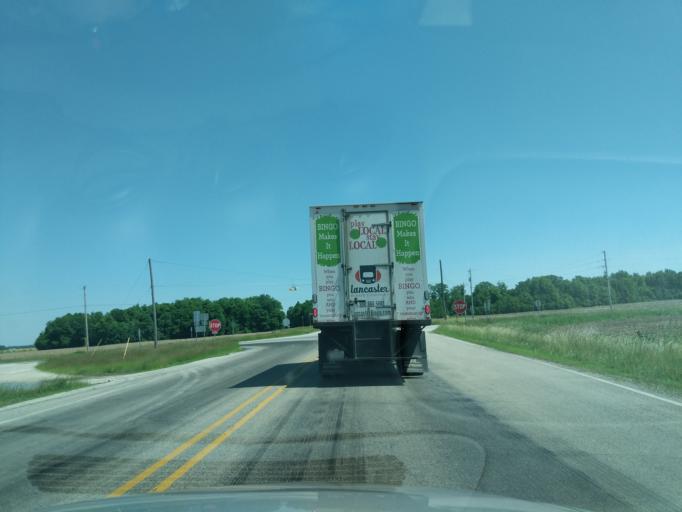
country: US
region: Indiana
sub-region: Huntington County
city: Roanoke
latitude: 41.0039
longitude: -85.4716
